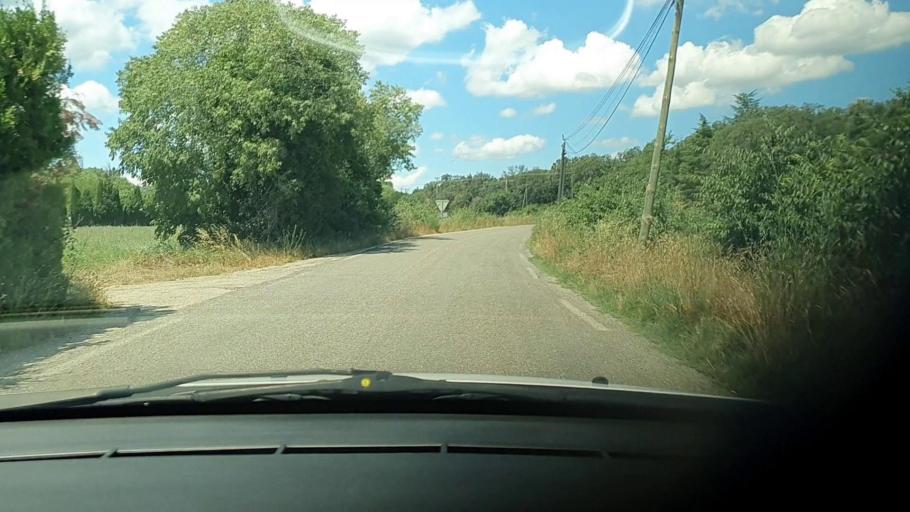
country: FR
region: Languedoc-Roussillon
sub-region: Departement du Gard
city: Uzes
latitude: 44.0031
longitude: 4.3939
